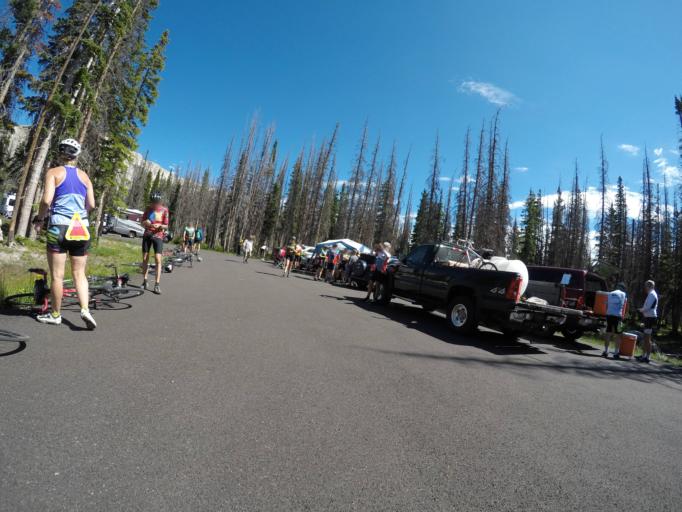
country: US
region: Wyoming
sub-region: Carbon County
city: Saratoga
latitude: 41.3296
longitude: -106.3235
